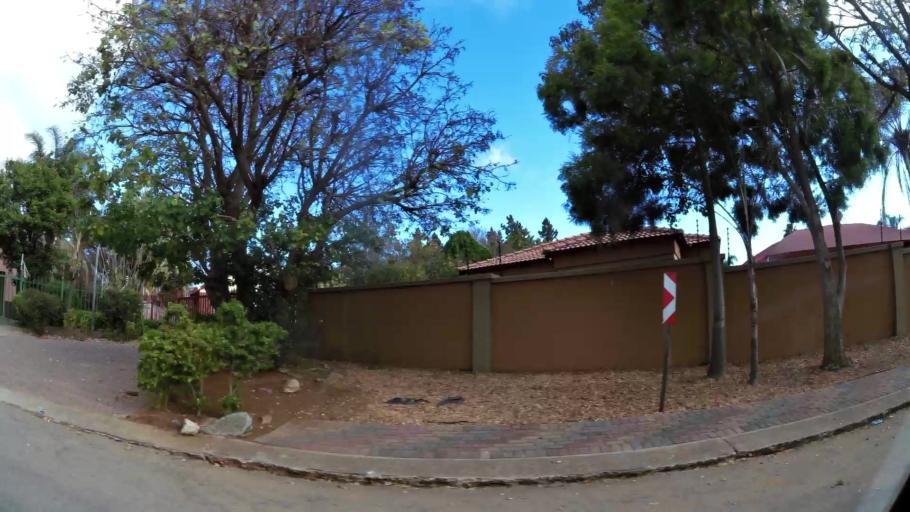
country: ZA
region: Limpopo
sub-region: Capricorn District Municipality
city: Polokwane
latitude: -23.9165
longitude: 29.4453
